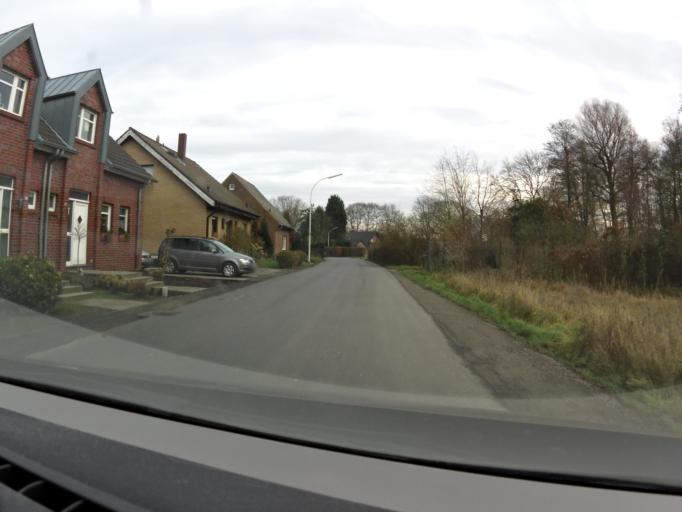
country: DE
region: North Rhine-Westphalia
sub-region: Regierungsbezirk Dusseldorf
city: Nettetal
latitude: 51.3126
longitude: 6.2567
